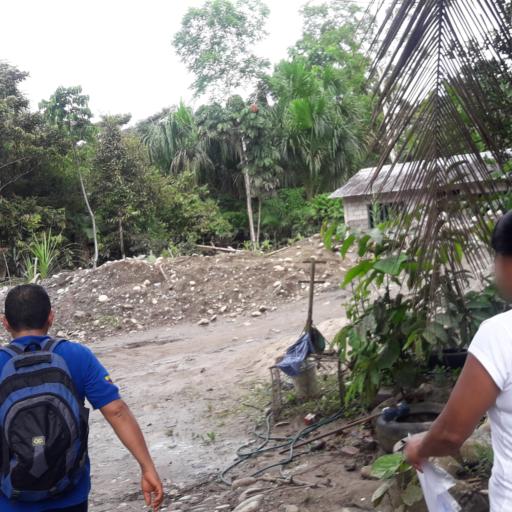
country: EC
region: Napo
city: Tena
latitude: -1.0351
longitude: -77.7484
